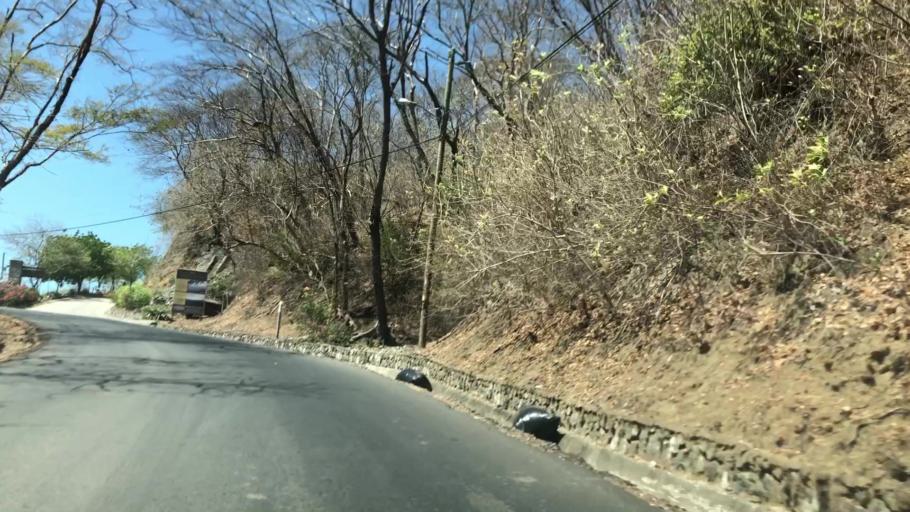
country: CR
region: Guanacaste
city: Belen
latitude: 10.3491
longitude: -85.8219
